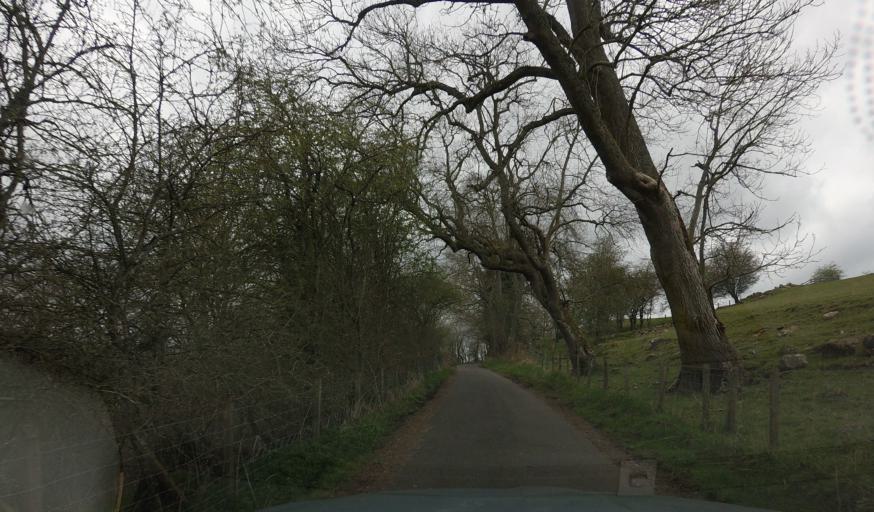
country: GB
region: Scotland
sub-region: Fife
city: Pathhead
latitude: 55.8424
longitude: -2.9949
